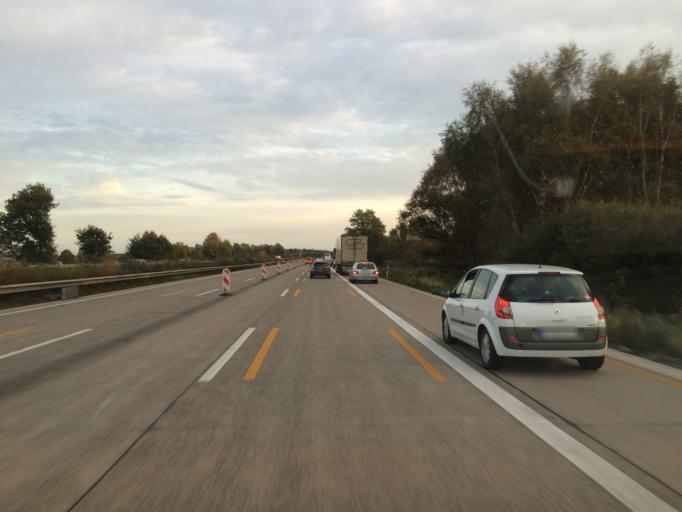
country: DE
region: Lower Saxony
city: Essel
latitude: 52.7216
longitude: 9.6802
